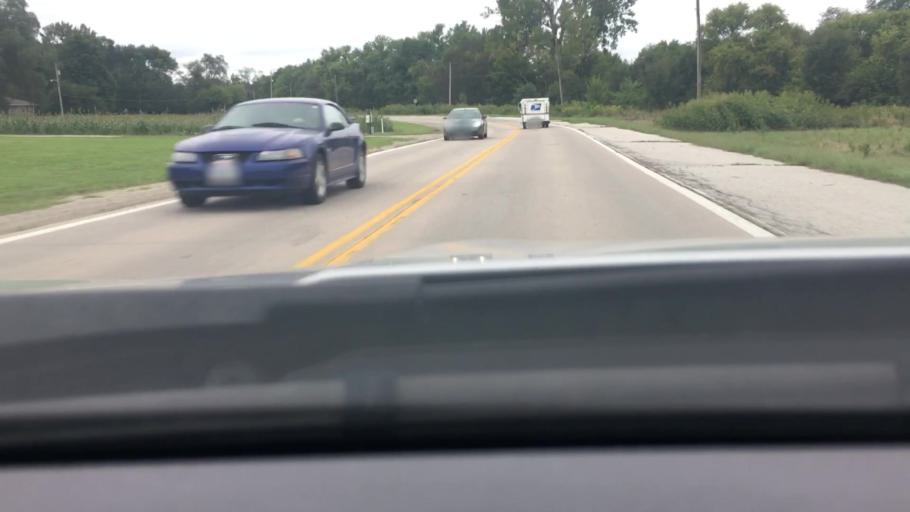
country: US
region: Iowa
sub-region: Pottawattamie County
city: Council Bluffs
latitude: 41.2592
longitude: -95.8064
